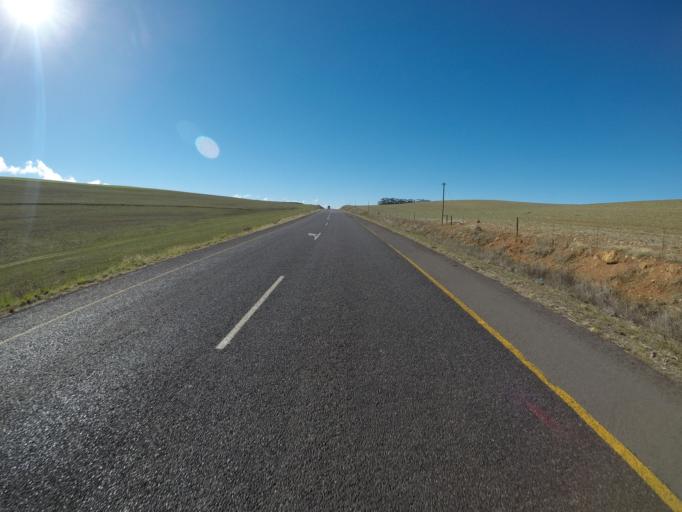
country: ZA
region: Western Cape
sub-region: Overberg District Municipality
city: Caledon
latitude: -34.1440
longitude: 19.4977
